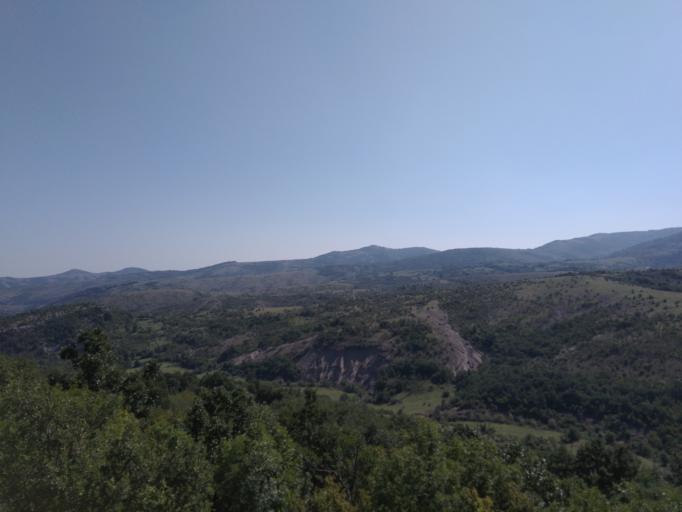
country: BG
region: Kurdzhali
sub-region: Obshtina Krumovgrad
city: Krumovgrad
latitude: 41.5155
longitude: 25.6647
